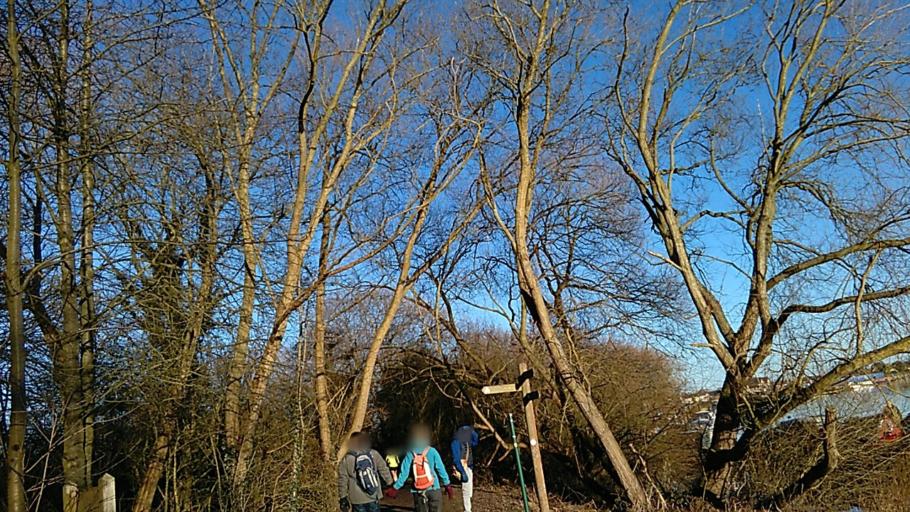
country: GB
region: England
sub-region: Nottinghamshire
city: Gotham
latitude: 52.9119
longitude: -1.2126
